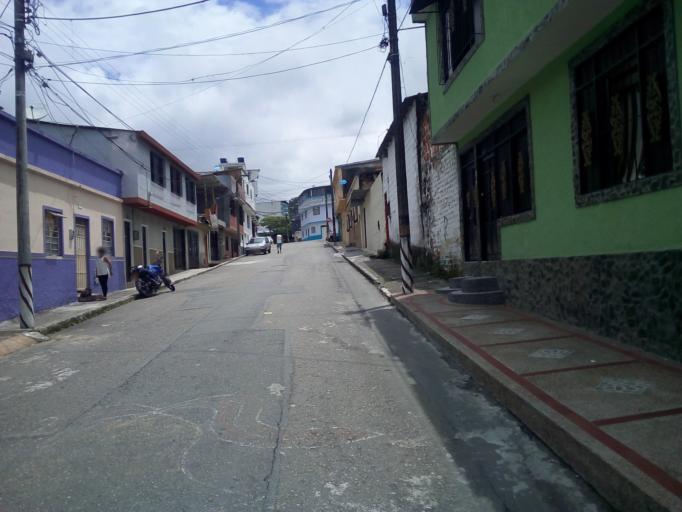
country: CO
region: Tolima
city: Ibague
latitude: 4.4517
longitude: -75.2415
